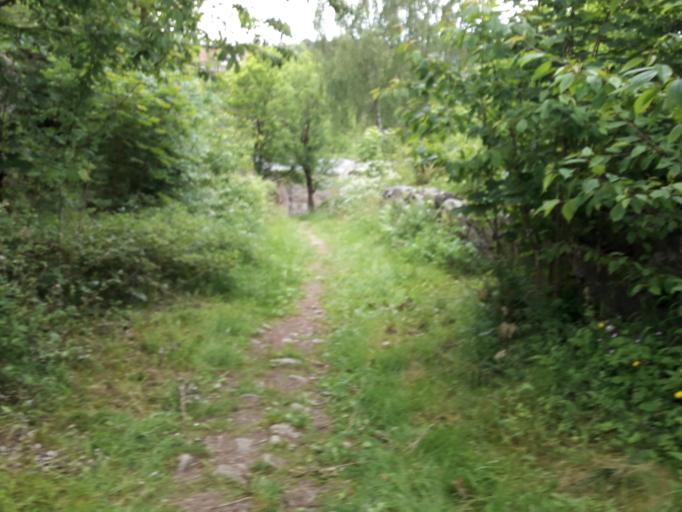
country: NO
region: Akershus
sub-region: Frogn
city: Drobak
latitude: 59.6754
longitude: 10.6073
